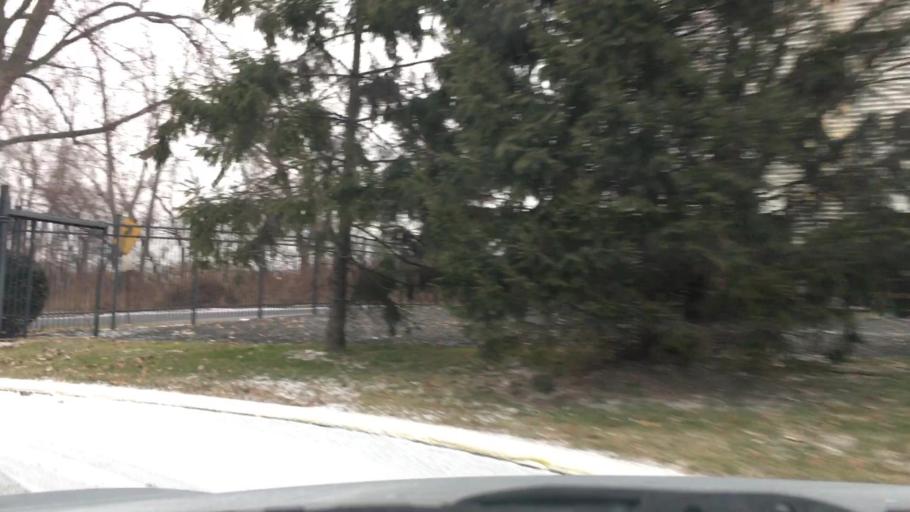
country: US
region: Massachusetts
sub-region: Hampden County
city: Springfield
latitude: 42.0912
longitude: -72.5910
